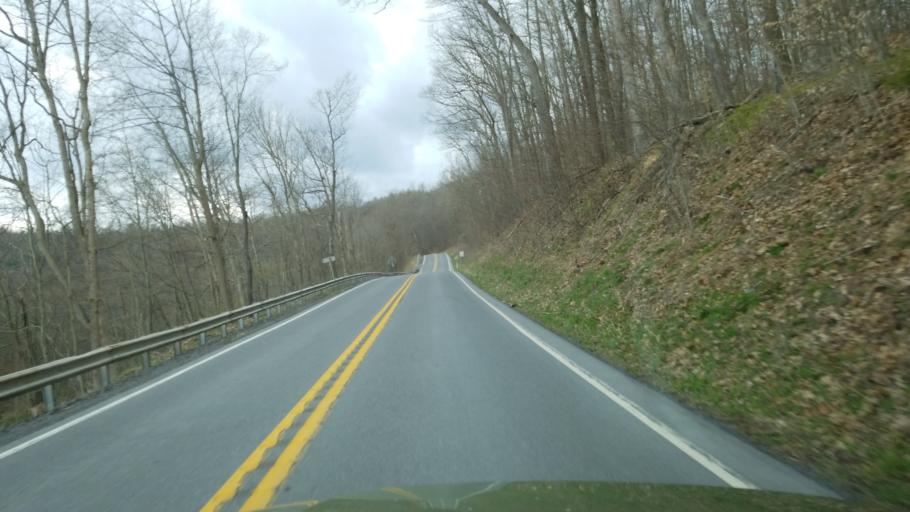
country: US
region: Pennsylvania
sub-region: Clearfield County
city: Curwensville
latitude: 40.8479
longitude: -78.4441
